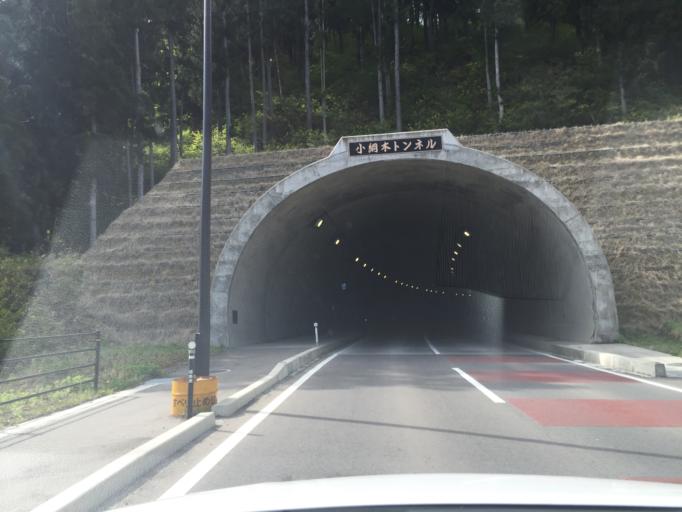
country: JP
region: Fukushima
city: Hobaramachi
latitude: 37.6384
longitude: 140.6436
